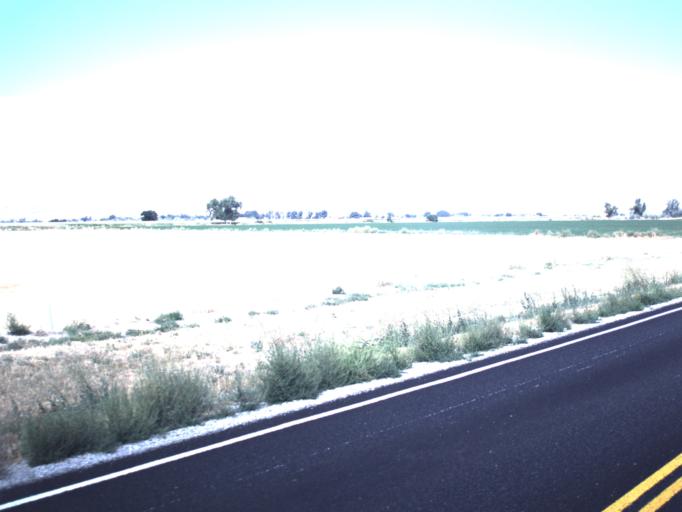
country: US
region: Utah
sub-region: Box Elder County
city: Elwood
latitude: 41.6424
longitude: -112.1306
